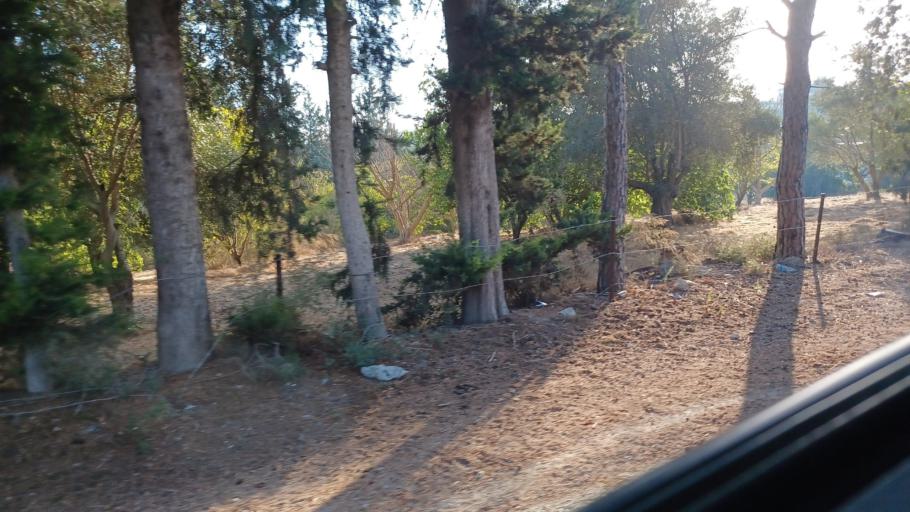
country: CY
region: Pafos
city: Mesogi
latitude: 34.8348
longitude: 32.4814
